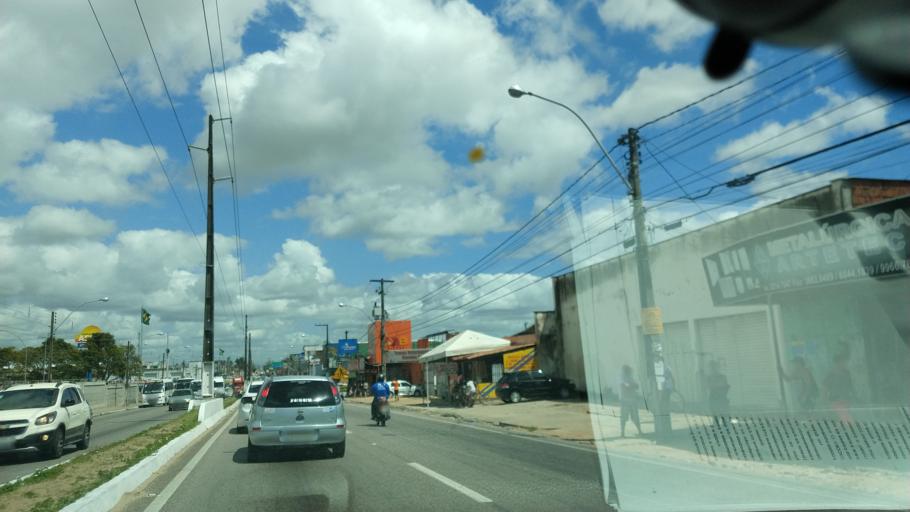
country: BR
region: Rio Grande do Norte
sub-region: Natal
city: Natal
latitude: -5.7717
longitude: -35.2644
